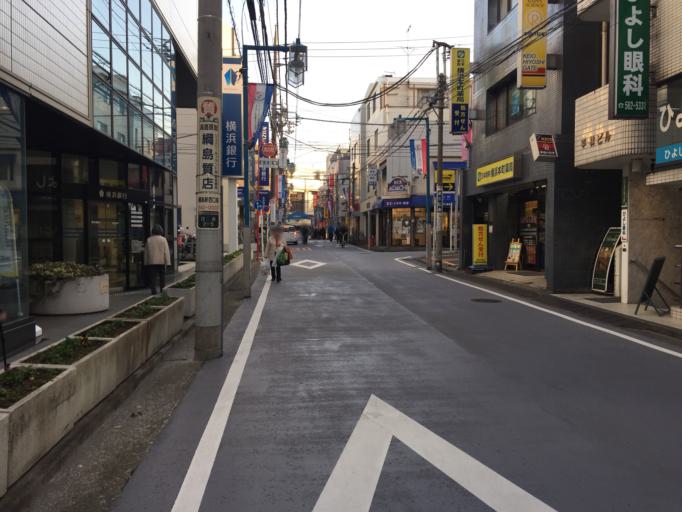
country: JP
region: Kanagawa
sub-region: Kawasaki-shi
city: Kawasaki
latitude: 35.5547
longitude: 139.6458
